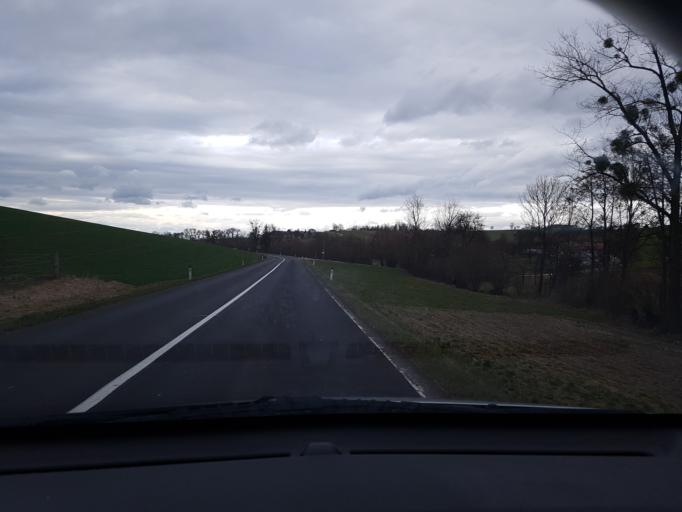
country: AT
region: Upper Austria
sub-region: Politischer Bezirk Linz-Land
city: Ansfelden
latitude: 48.1794
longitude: 14.2736
